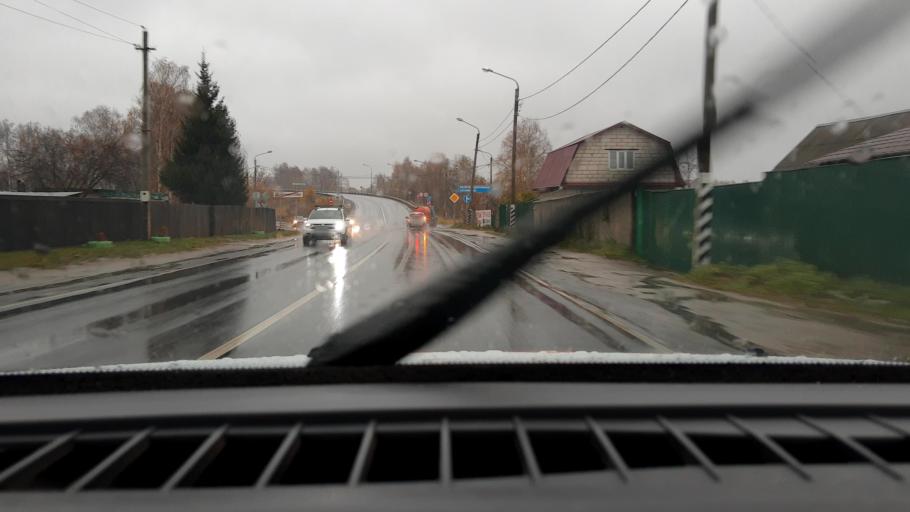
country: RU
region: Nizjnij Novgorod
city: Sitniki
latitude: 56.4652
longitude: 44.0363
